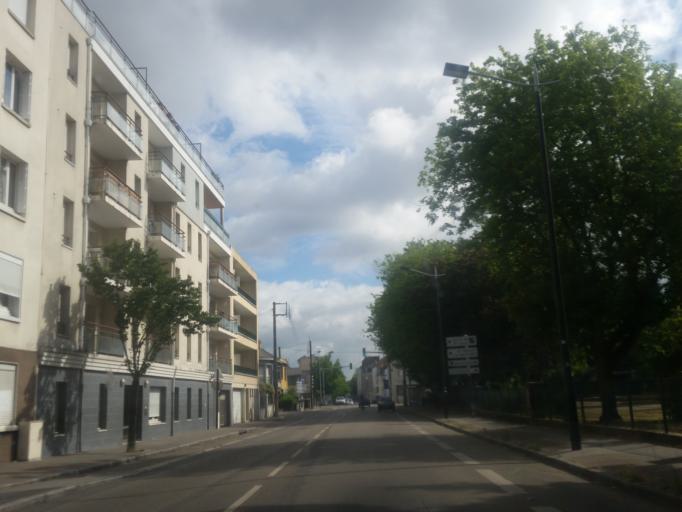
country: FR
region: Pays de la Loire
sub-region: Departement de la Loire-Atlantique
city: Nantes
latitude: 47.2276
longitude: -1.5275
